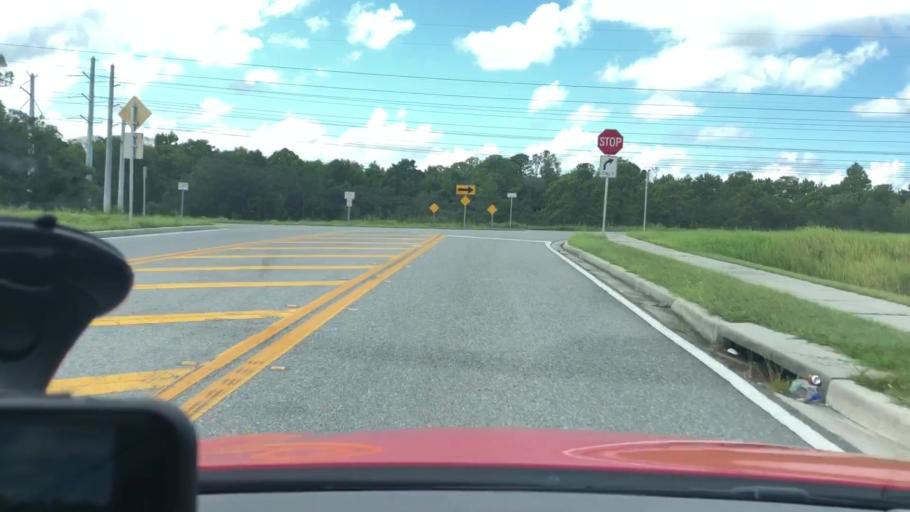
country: US
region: Florida
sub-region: Volusia County
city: Daytona Beach
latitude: 29.1961
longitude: -81.0968
